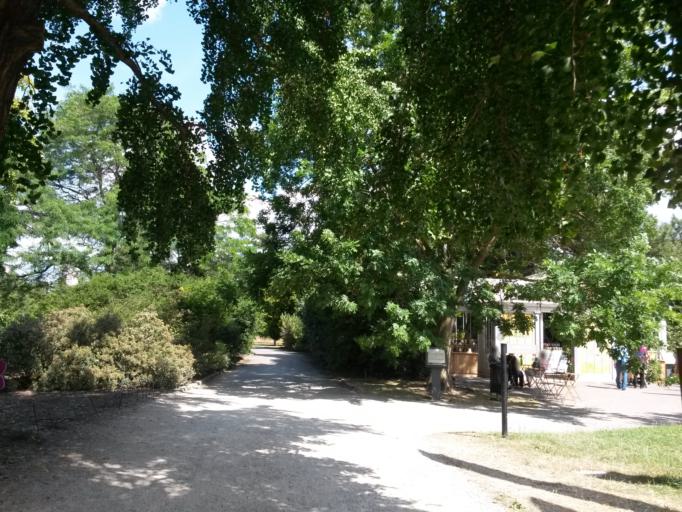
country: GB
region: England
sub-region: Greater London
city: Brentford
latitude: 51.4826
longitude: -0.2914
